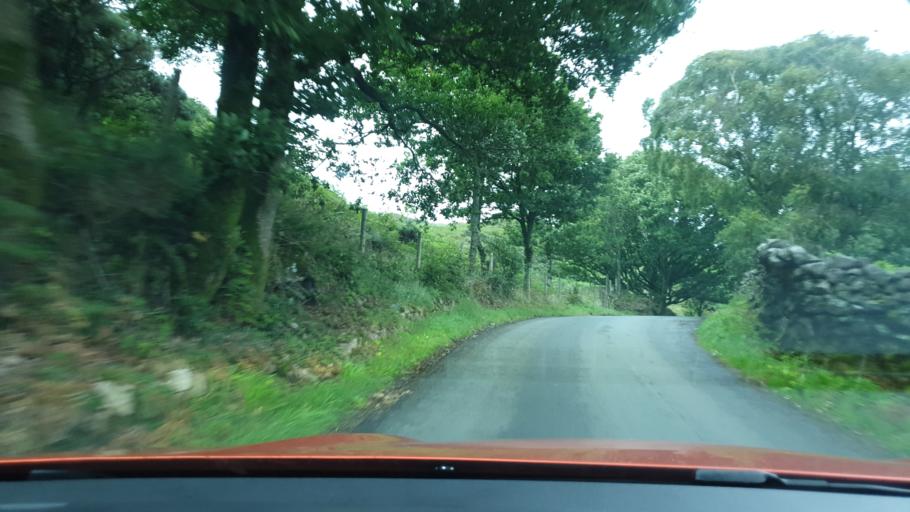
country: GB
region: England
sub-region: Cumbria
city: Seascale
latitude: 54.3801
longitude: -3.3081
